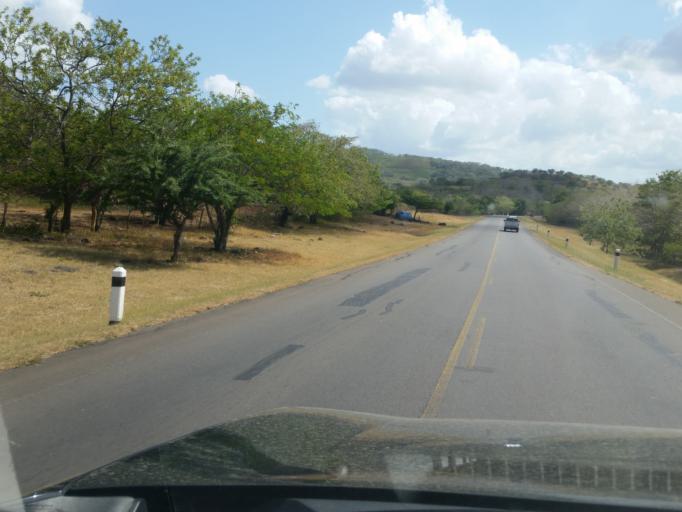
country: NI
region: Chontales
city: Comalapa
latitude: 12.2248
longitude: -85.6424
